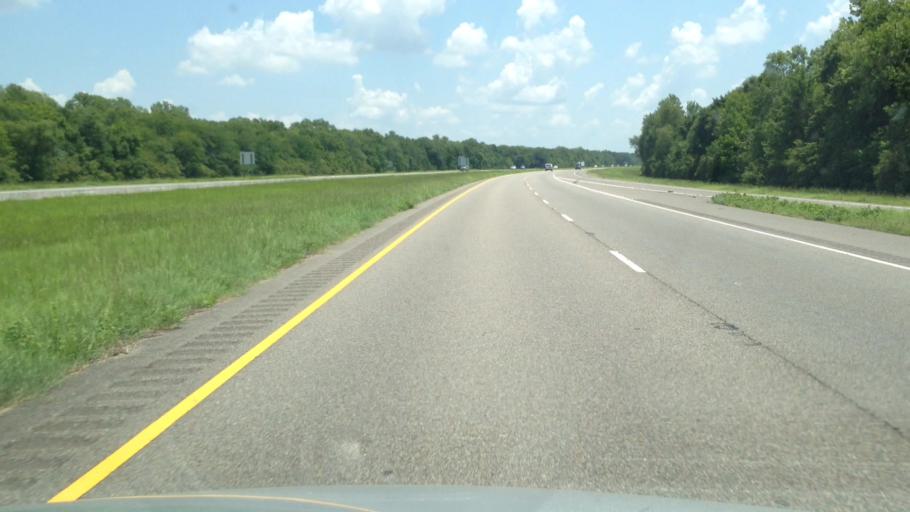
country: US
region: Louisiana
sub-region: Avoyelles Parish
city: Bunkie
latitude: 30.9849
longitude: -92.3049
